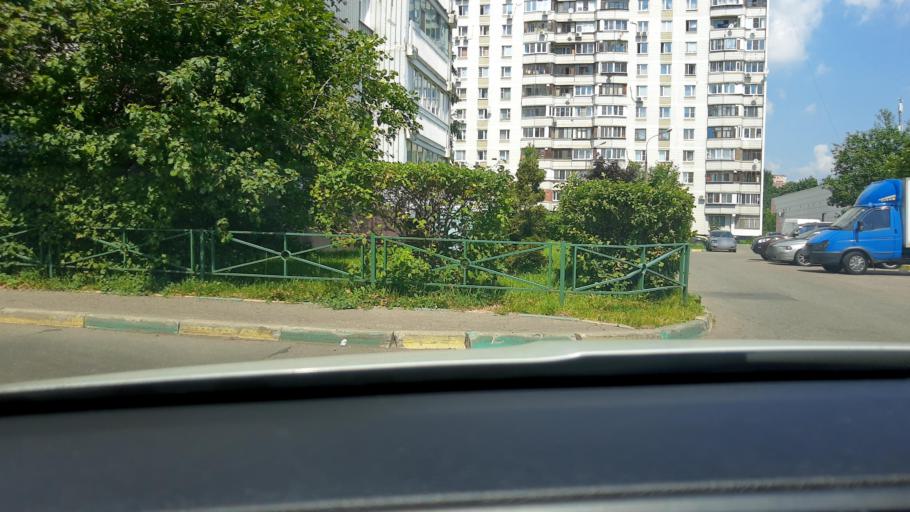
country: RU
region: Moskovskaya
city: Moskovskiy
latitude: 55.5975
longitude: 37.3539
